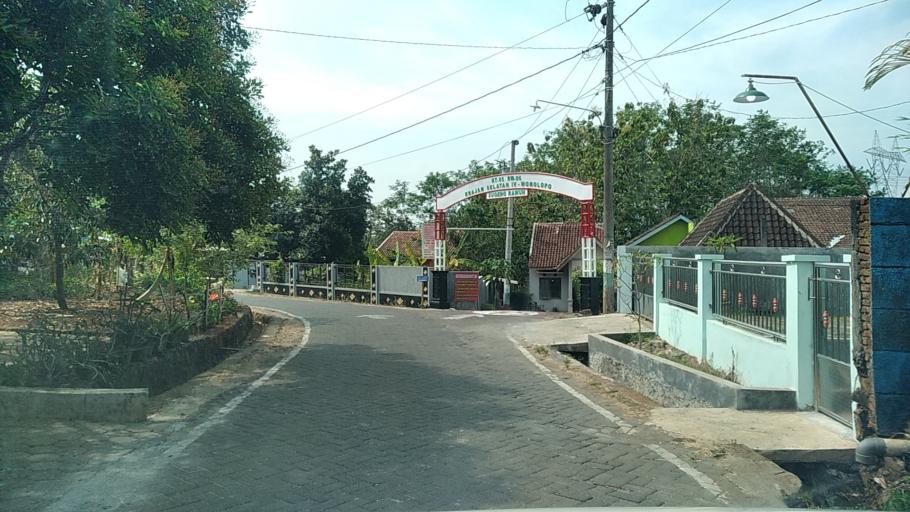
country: ID
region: Central Java
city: Ungaran
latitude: -7.0602
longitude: 110.3096
